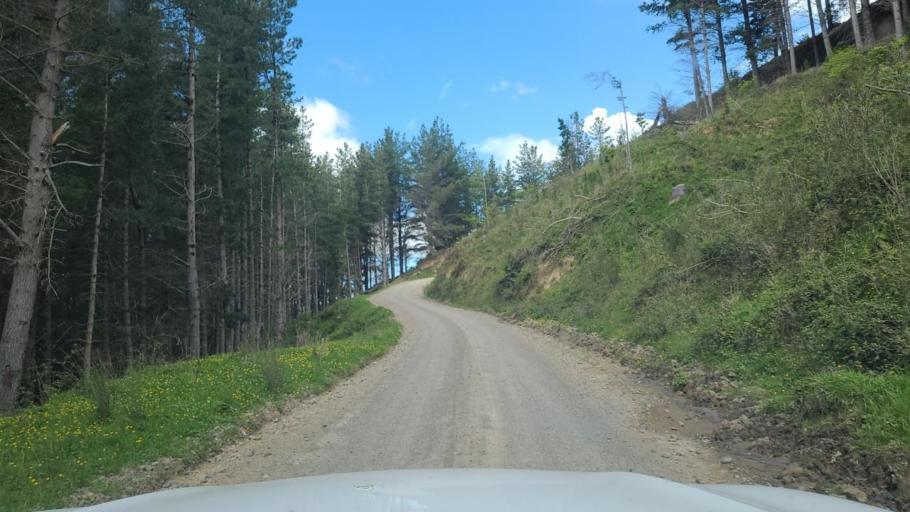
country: NZ
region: Hawke's Bay
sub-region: Napier City
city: Taradale
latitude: -39.2674
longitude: 176.6517
